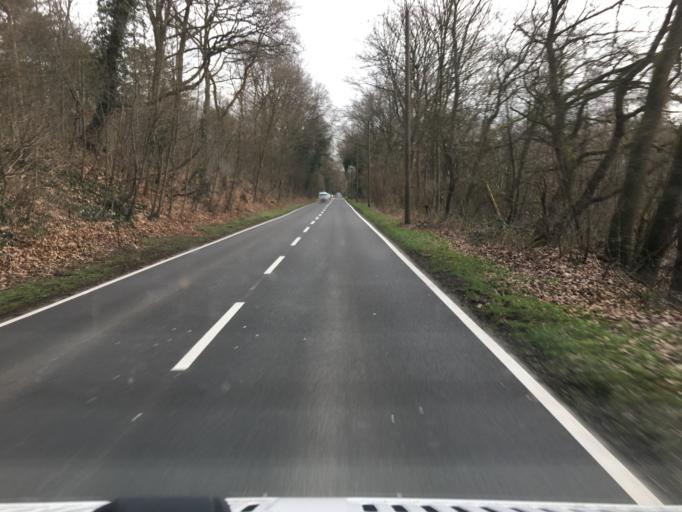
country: DE
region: North Rhine-Westphalia
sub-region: Regierungsbezirk Koln
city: Merheim
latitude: 50.9884
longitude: 7.0627
